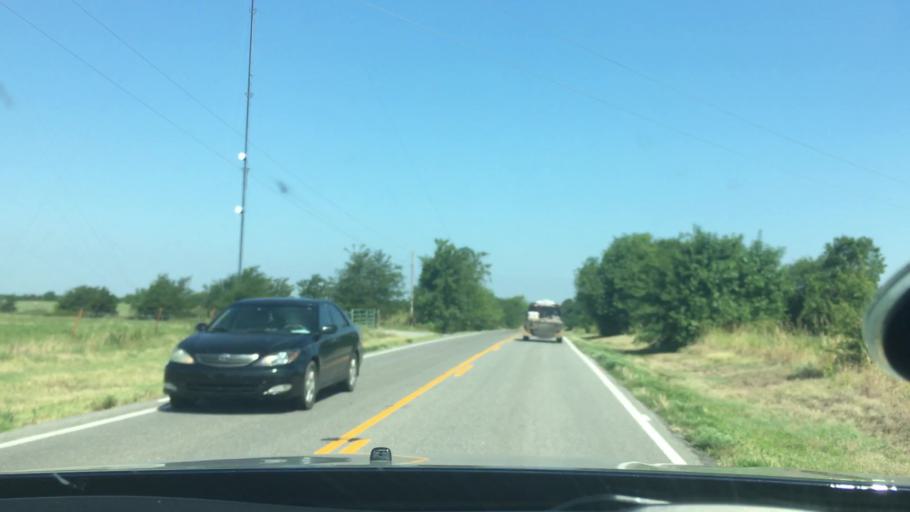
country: US
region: Oklahoma
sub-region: Johnston County
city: Tishomingo
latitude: 34.1937
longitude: -96.5354
